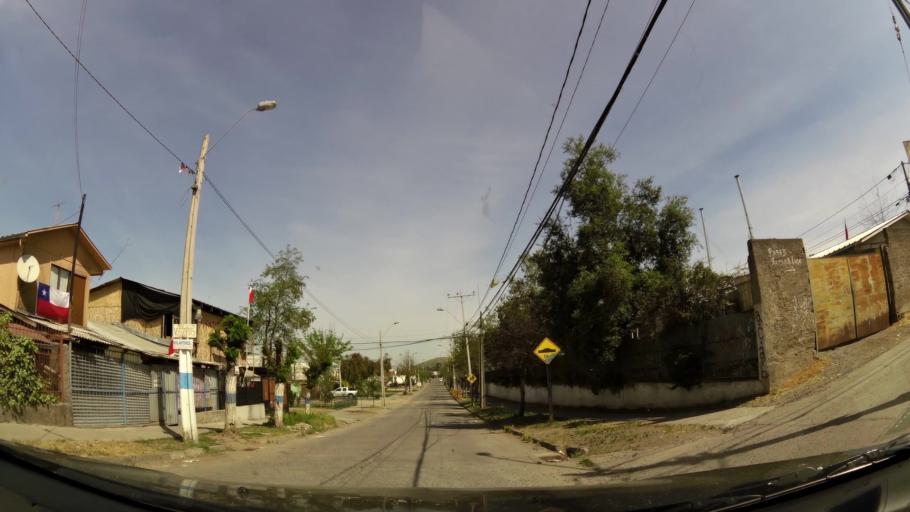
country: CL
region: Santiago Metropolitan
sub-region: Provincia de Cordillera
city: Puente Alto
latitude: -33.6221
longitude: -70.5819
